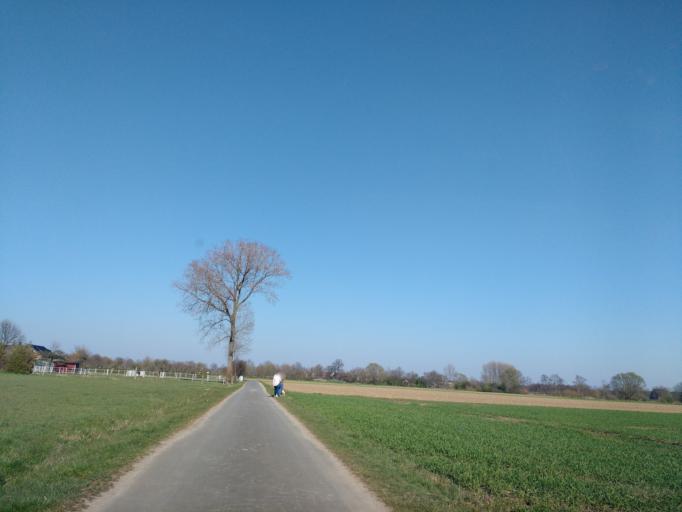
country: DE
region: North Rhine-Westphalia
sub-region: Regierungsbezirk Detmold
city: Delbruck
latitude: 51.7232
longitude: 8.5536
